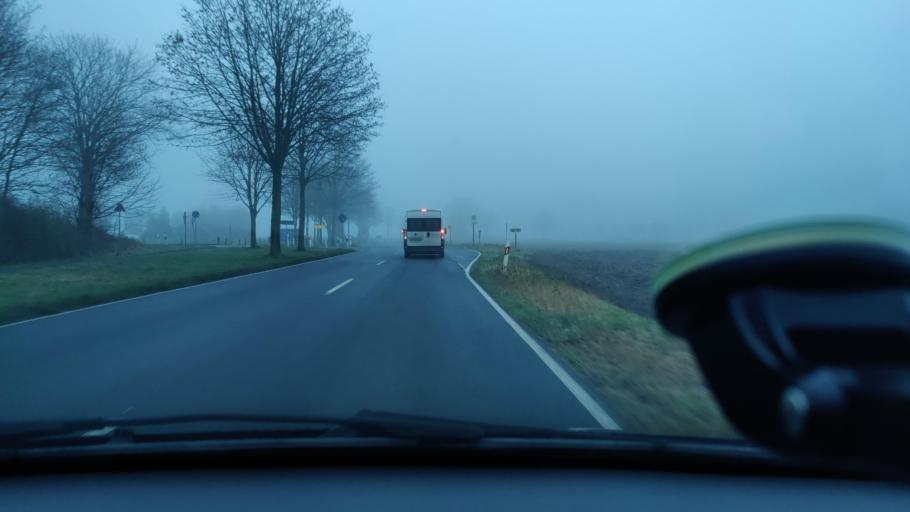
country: DE
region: North Rhine-Westphalia
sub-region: Regierungsbezirk Dusseldorf
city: Mehrhoog
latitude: 51.7021
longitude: 6.4883
